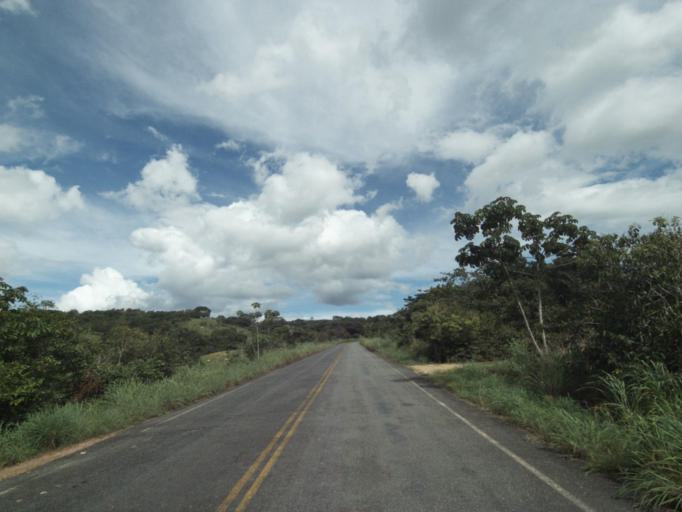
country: BR
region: Goias
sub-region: Pirenopolis
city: Pirenopolis
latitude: -15.7773
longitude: -49.0520
